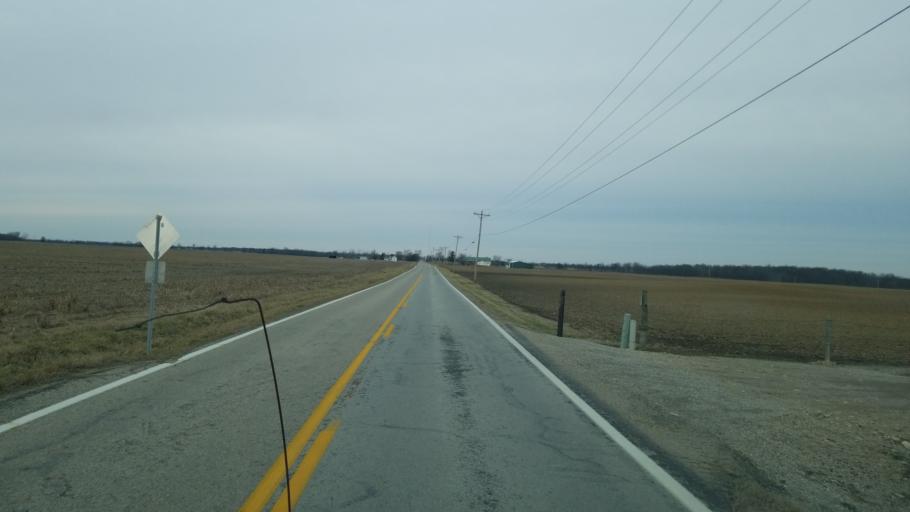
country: US
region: Ohio
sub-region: Pickaway County
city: Williamsport
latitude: 39.5279
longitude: -83.1252
